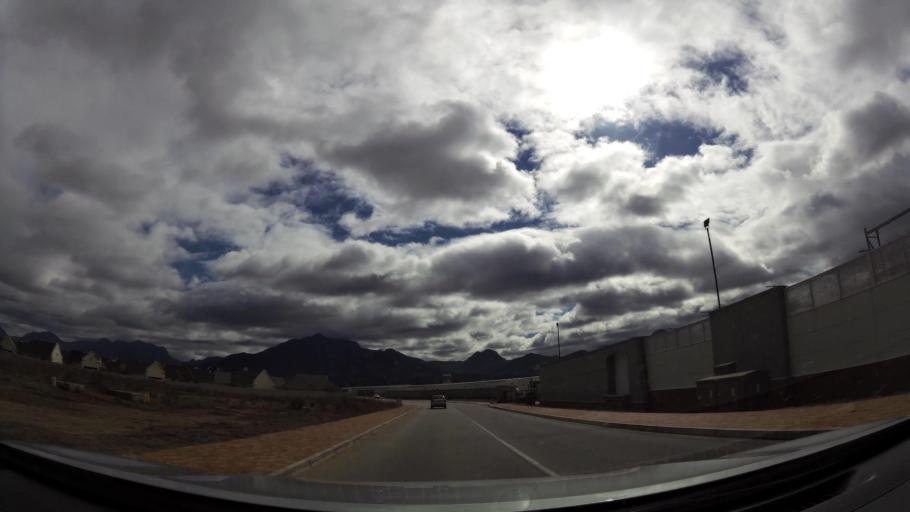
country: ZA
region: Western Cape
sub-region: Eden District Municipality
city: George
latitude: -33.9853
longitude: 22.4985
